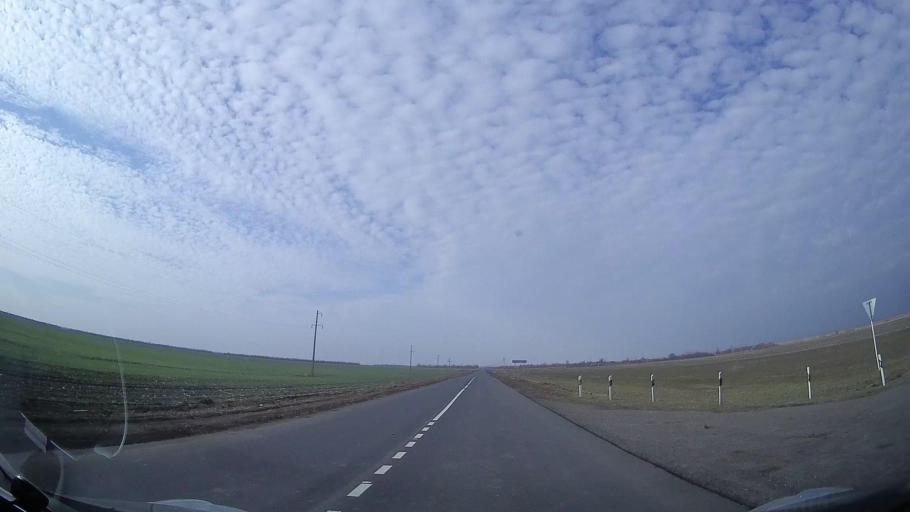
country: RU
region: Rostov
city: Veselyy
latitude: 47.0560
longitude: 40.8666
